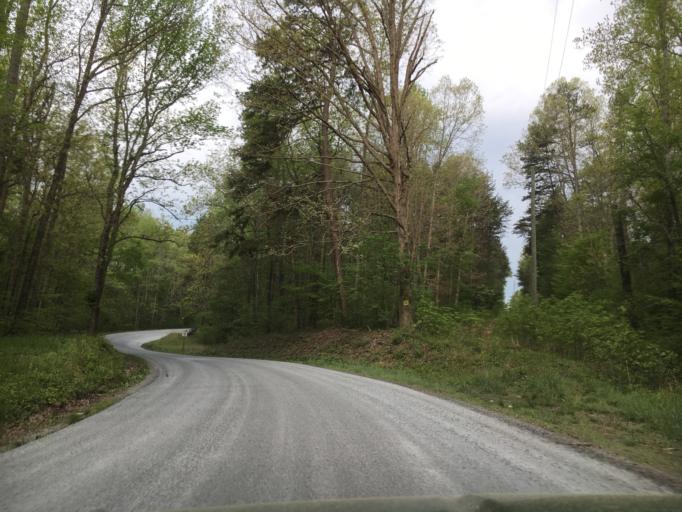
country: US
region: Virginia
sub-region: Campbell County
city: Brookneal
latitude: 36.9456
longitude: -78.9534
